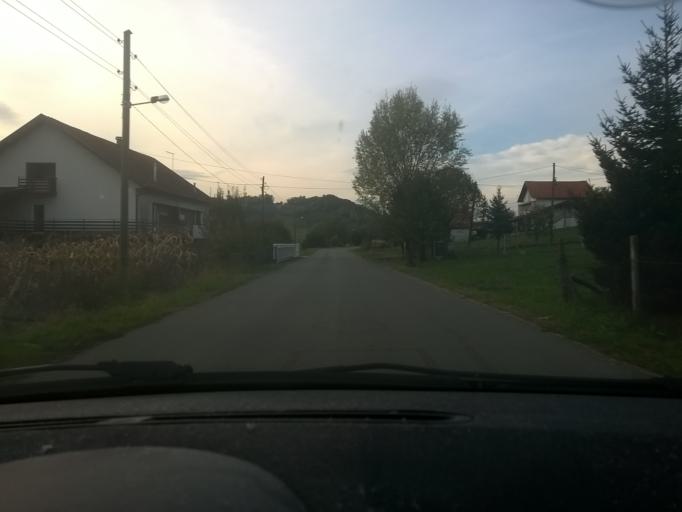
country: HR
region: Krapinsko-Zagorska
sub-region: Grad Krapina
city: Krapina
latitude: 46.1124
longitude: 15.8661
